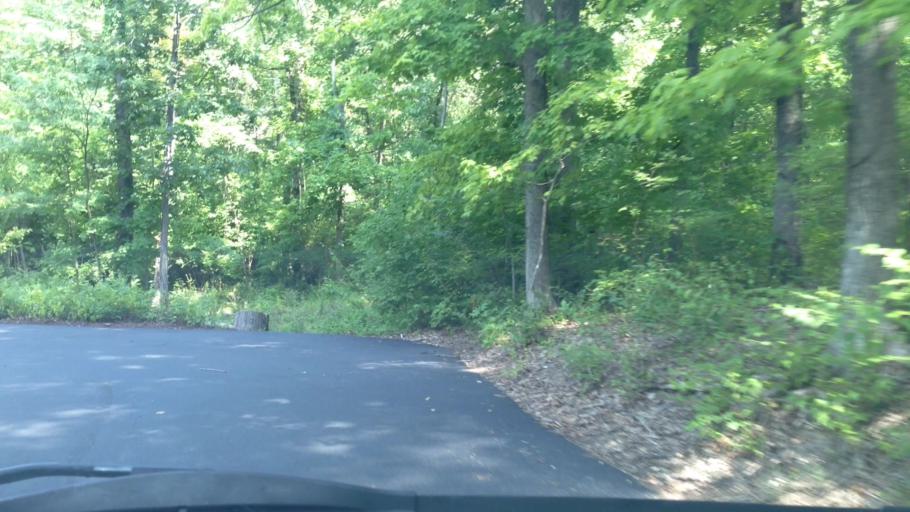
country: US
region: Missouri
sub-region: Saint Louis County
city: Des Peres
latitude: 38.5827
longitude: -90.4432
